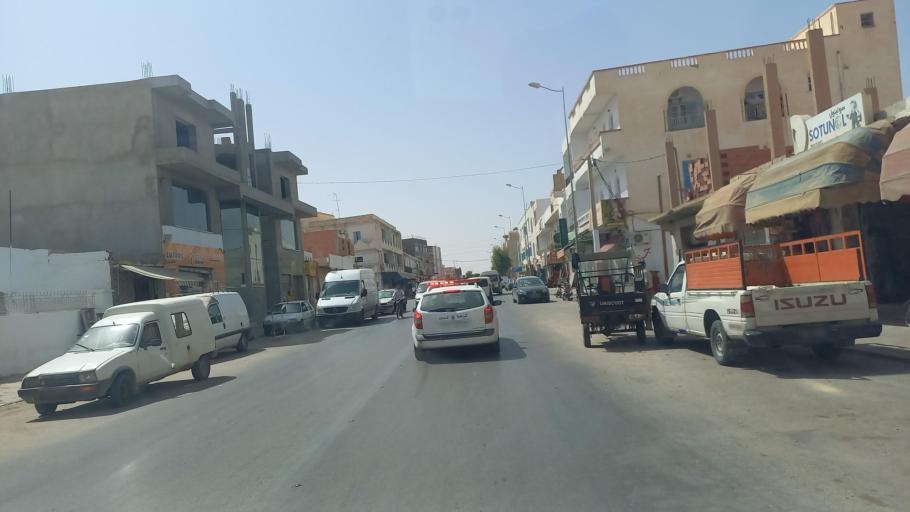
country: TN
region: Madanin
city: Medenine
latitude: 33.3343
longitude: 10.4855
